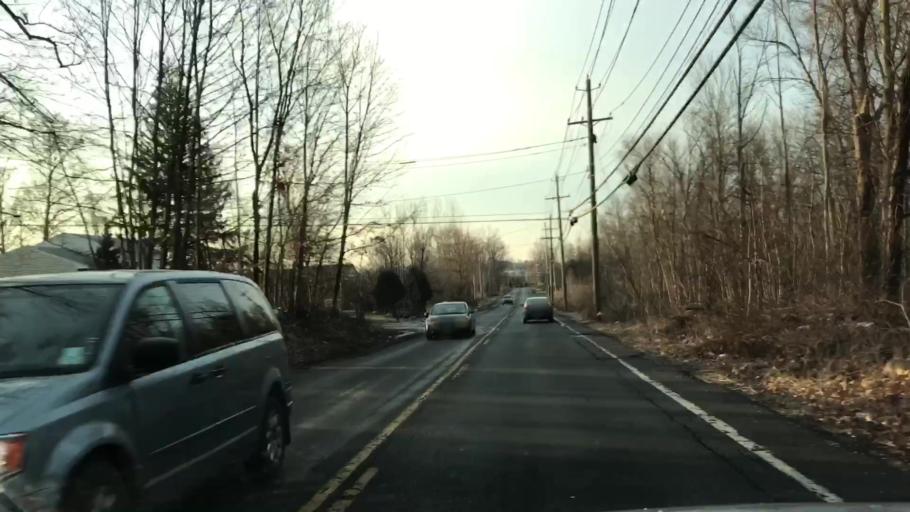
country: US
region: New York
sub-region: Rockland County
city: New Hempstead
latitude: 41.1472
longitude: -74.0341
